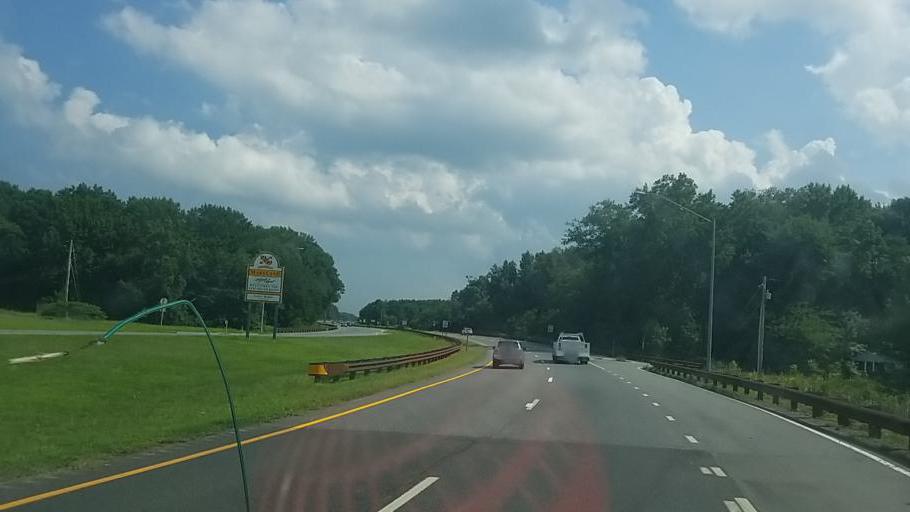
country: US
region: Delaware
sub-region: Sussex County
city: Selbyville
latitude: 38.4513
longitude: -75.2332
